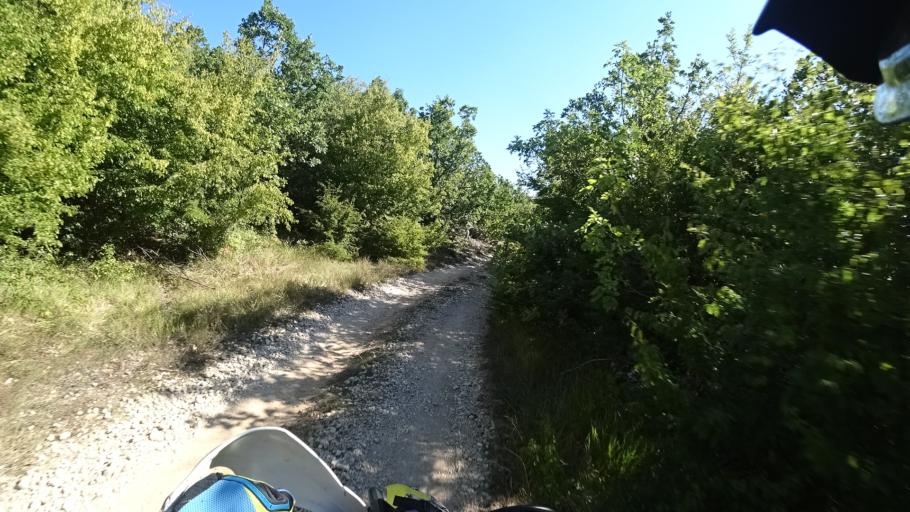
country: HR
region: Splitsko-Dalmatinska
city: Hrvace
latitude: 43.8933
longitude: 16.5218
